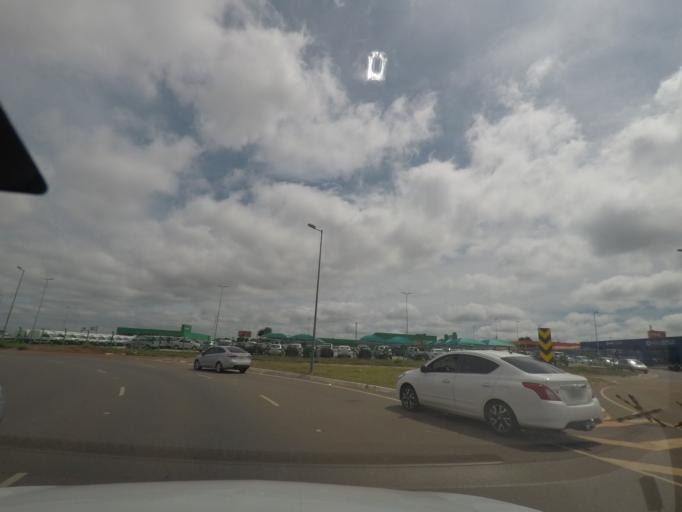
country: BR
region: Goias
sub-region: Goiania
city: Goiania
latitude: -16.6293
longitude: -49.2081
